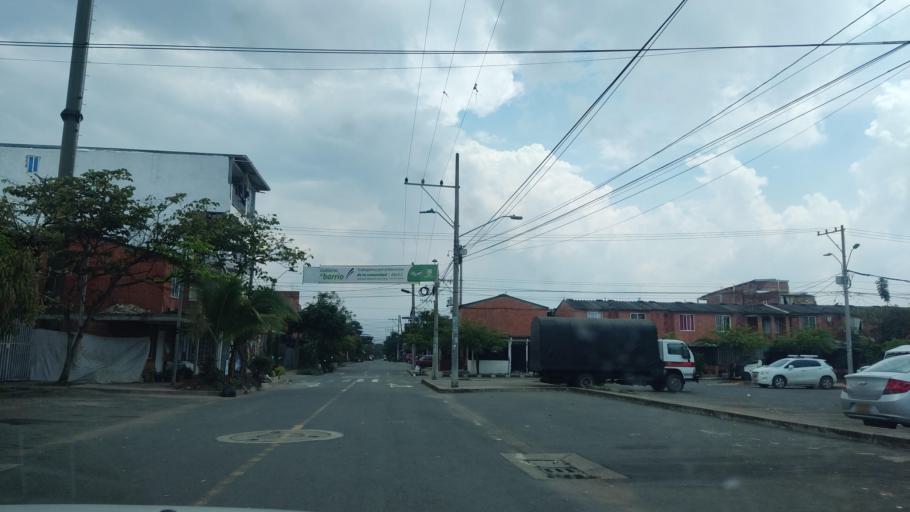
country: CO
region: Valle del Cauca
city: Cali
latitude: 3.3934
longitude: -76.5054
